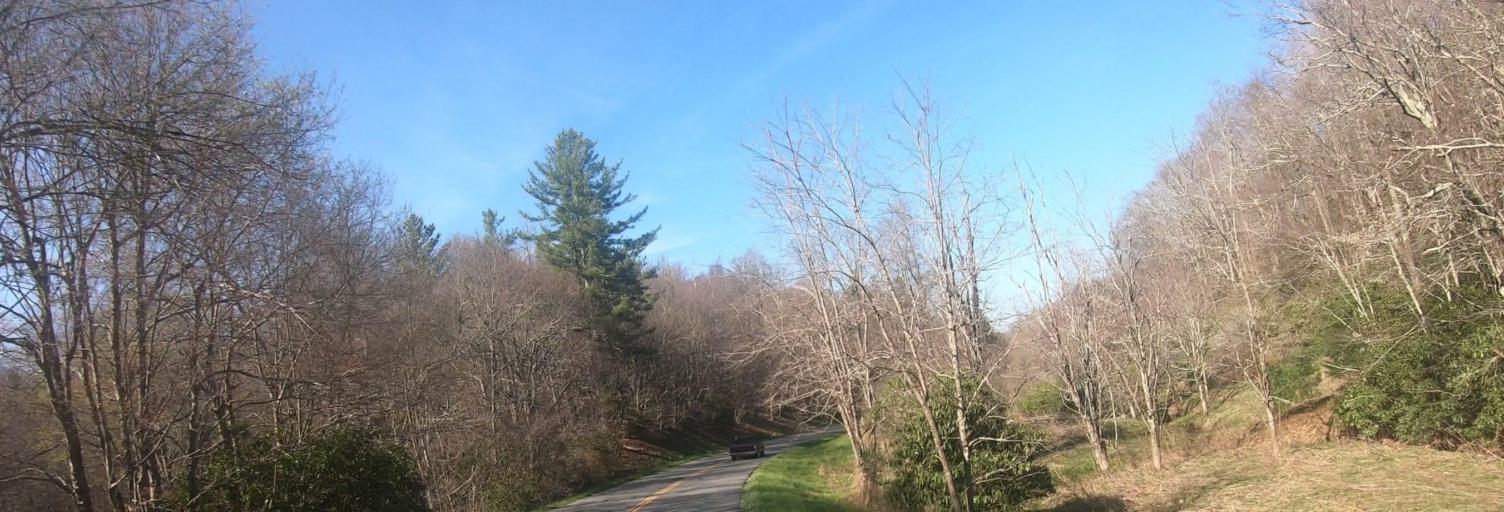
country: US
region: North Carolina
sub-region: Watauga County
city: Blowing Rock
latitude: 36.1636
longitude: -81.6207
